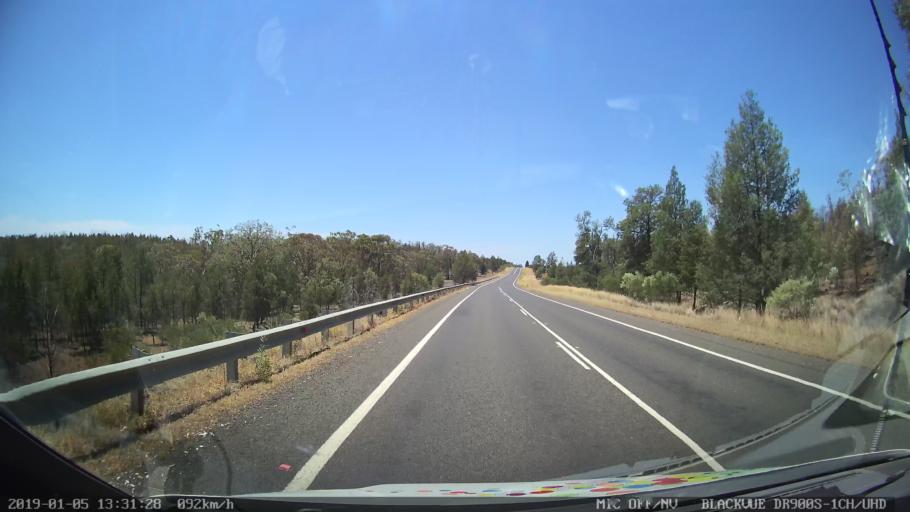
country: AU
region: New South Wales
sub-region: Gunnedah
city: Gunnedah
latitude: -31.0108
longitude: 150.0843
